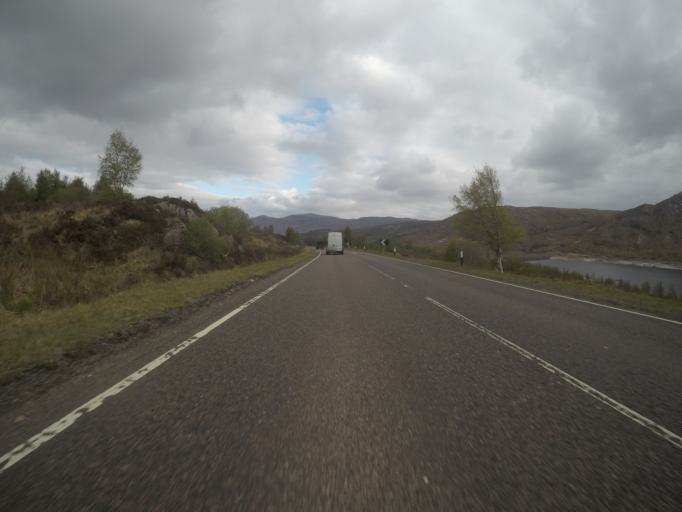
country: GB
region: Scotland
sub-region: Highland
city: Spean Bridge
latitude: 57.1474
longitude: -5.0069
